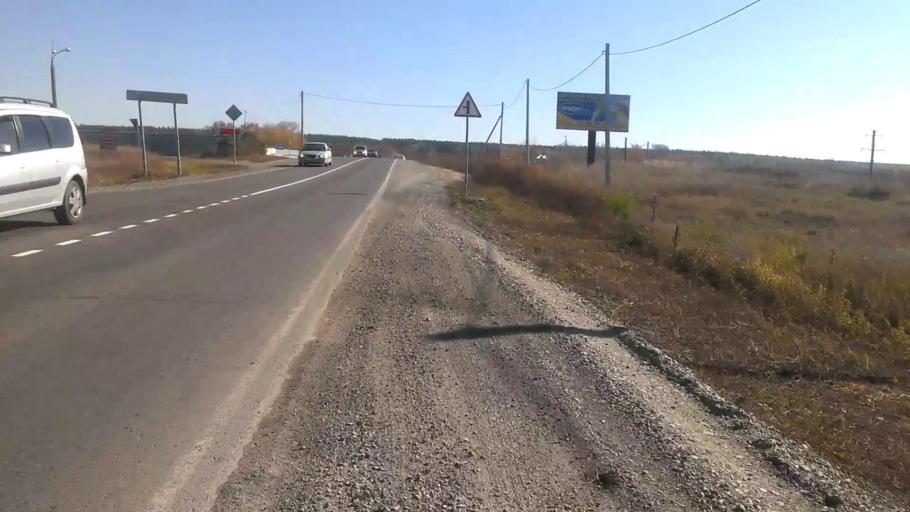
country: RU
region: Altai Krai
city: Sannikovo
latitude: 53.3138
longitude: 83.9619
